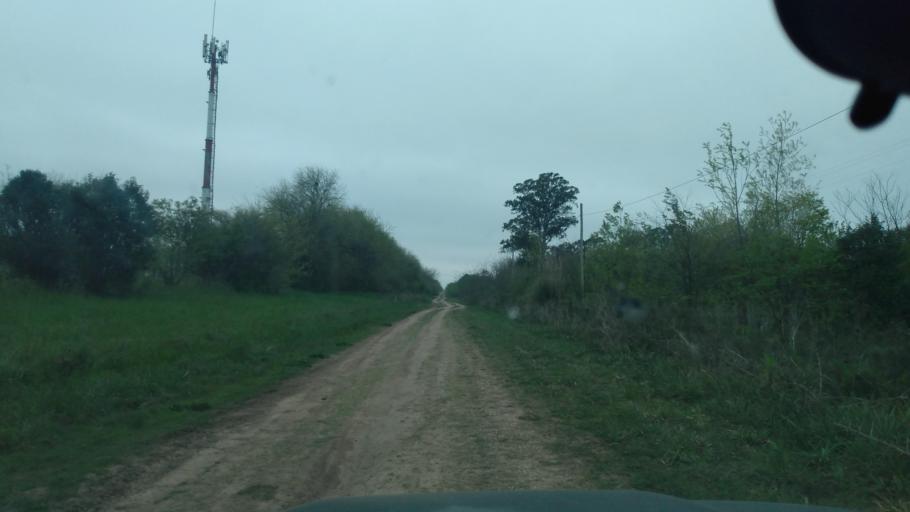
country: AR
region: Buenos Aires
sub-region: Partido de Lujan
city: Lujan
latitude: -34.5436
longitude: -59.2122
